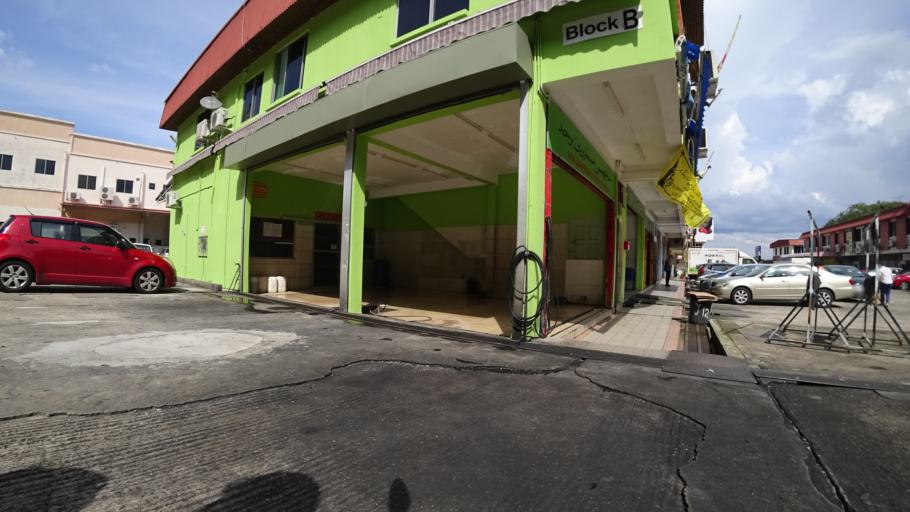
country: BN
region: Brunei and Muara
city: Bandar Seri Begawan
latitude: 4.8575
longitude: 114.8910
